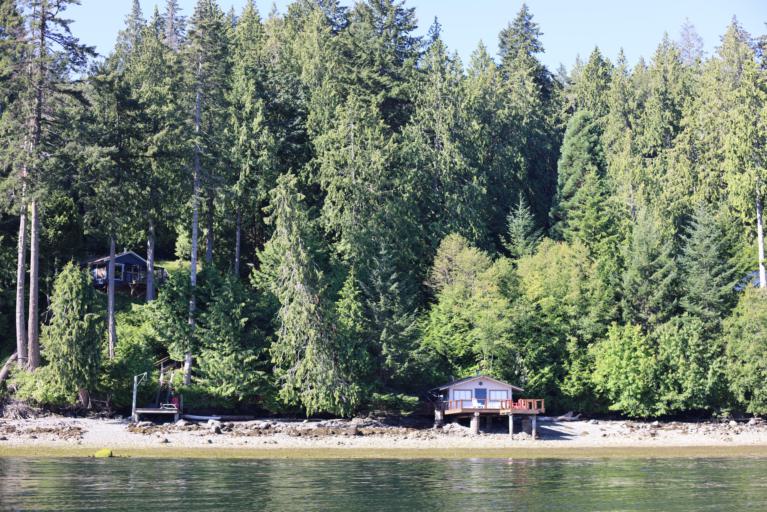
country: CA
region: British Columbia
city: North Cowichan
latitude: 48.8016
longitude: -123.5691
